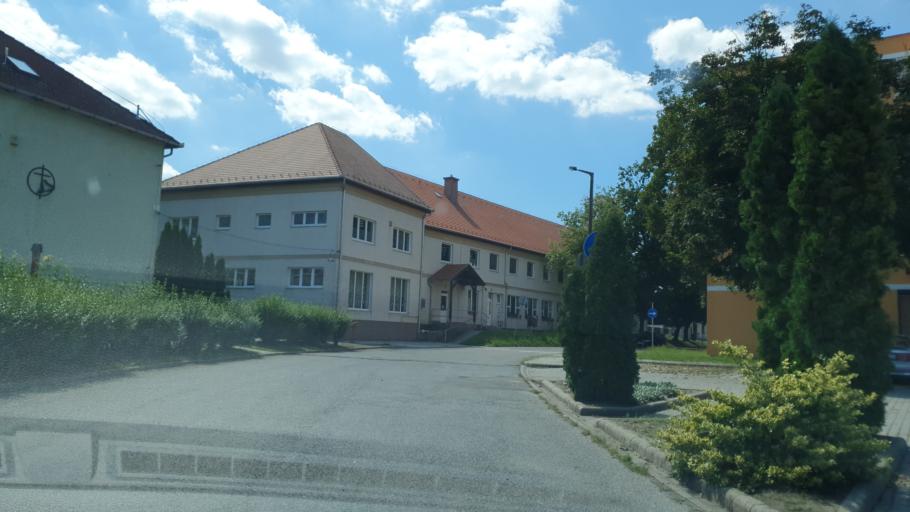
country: HU
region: Nograd
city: Szecseny
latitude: 48.0789
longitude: 19.5220
